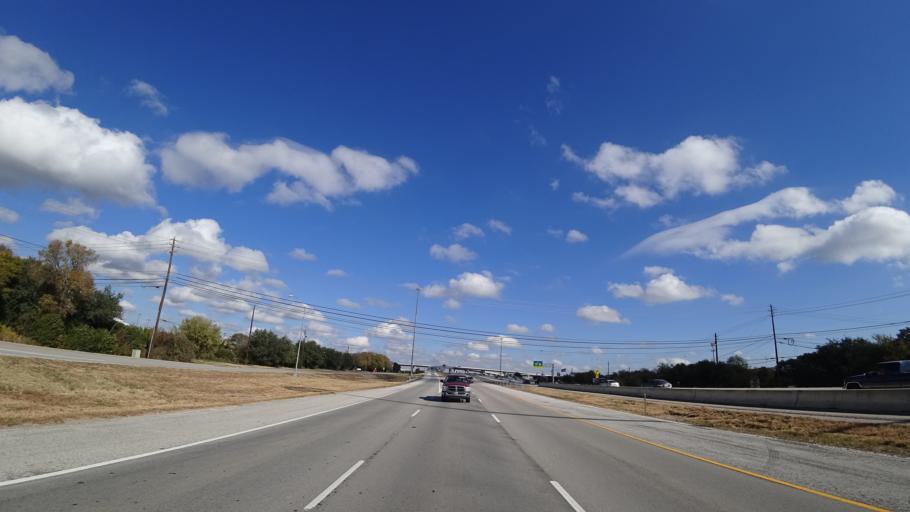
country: US
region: Texas
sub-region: Travis County
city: Rollingwood
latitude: 30.2307
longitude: -97.8276
